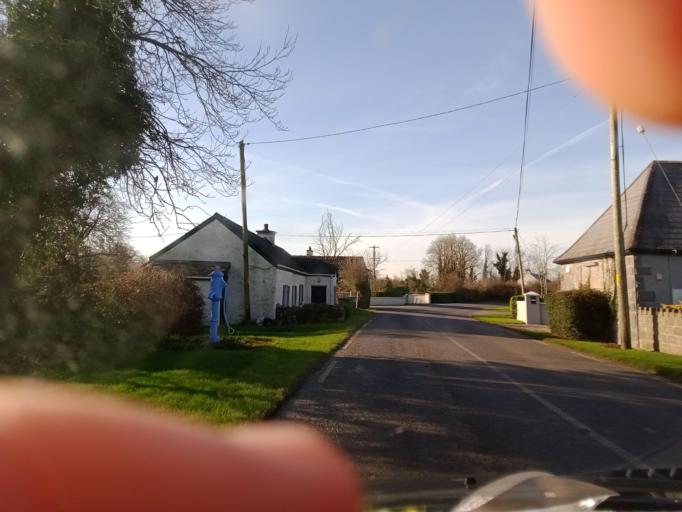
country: IE
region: Leinster
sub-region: Kilkenny
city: Callan
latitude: 52.5681
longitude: -7.4323
